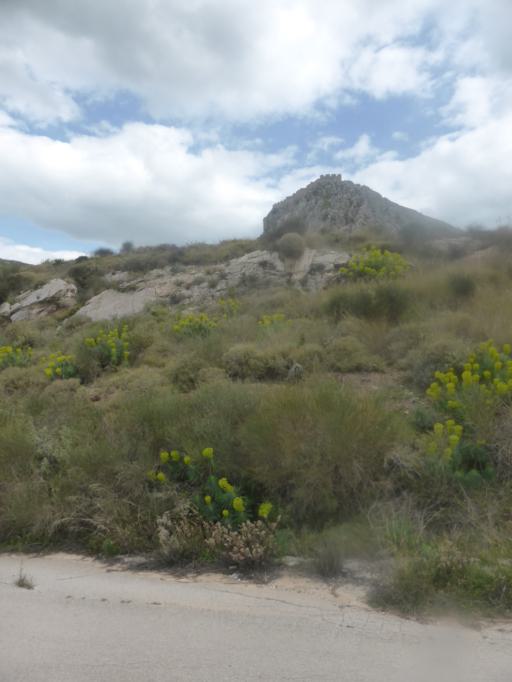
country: GR
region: Peloponnese
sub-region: Nomos Korinthias
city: Arkhaia Korinthos
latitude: 37.8892
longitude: 22.8661
